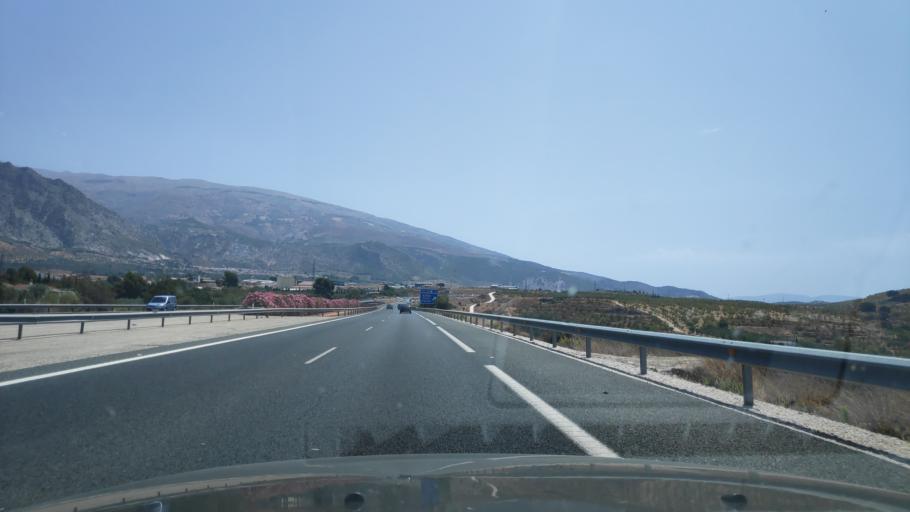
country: ES
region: Andalusia
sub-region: Provincia de Granada
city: Durcal
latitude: 36.9807
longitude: -3.5735
